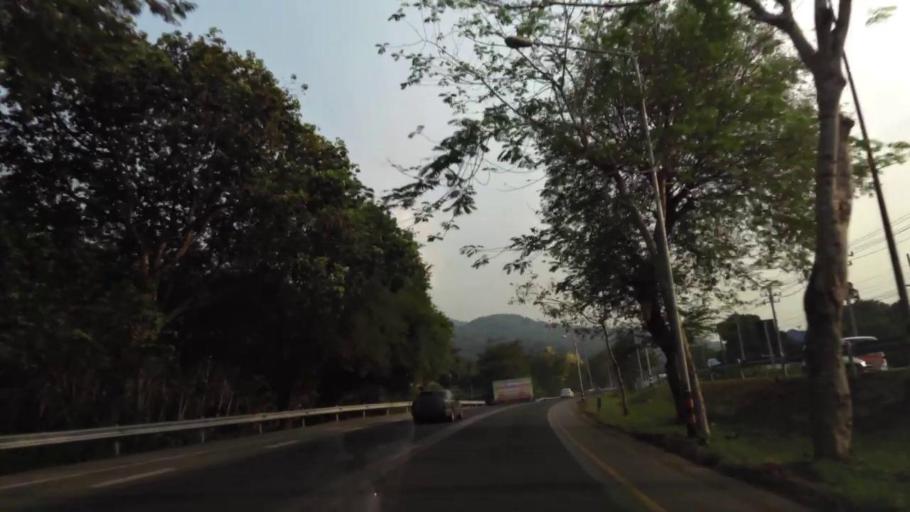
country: TH
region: Chanthaburi
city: Chanthaburi
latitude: 12.5747
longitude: 102.1617
